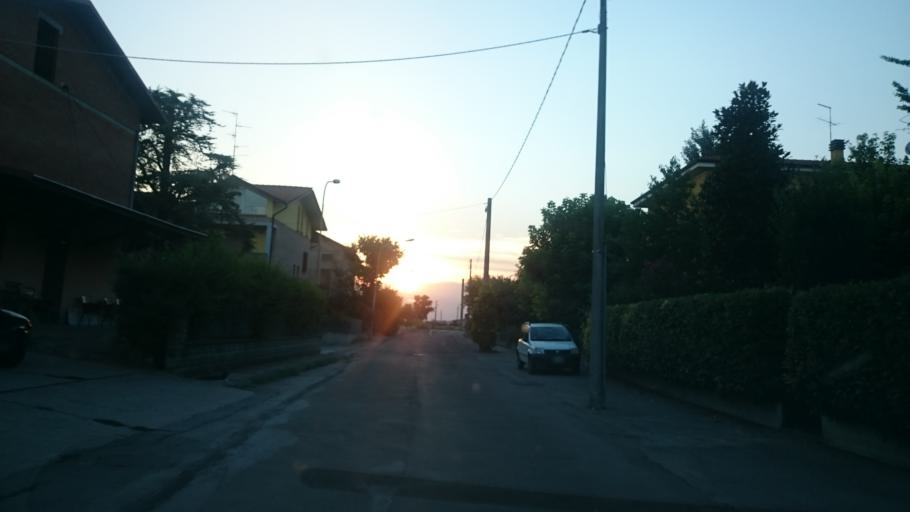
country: IT
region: Emilia-Romagna
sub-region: Provincia di Reggio Emilia
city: Arceto
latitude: 44.6230
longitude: 10.7259
